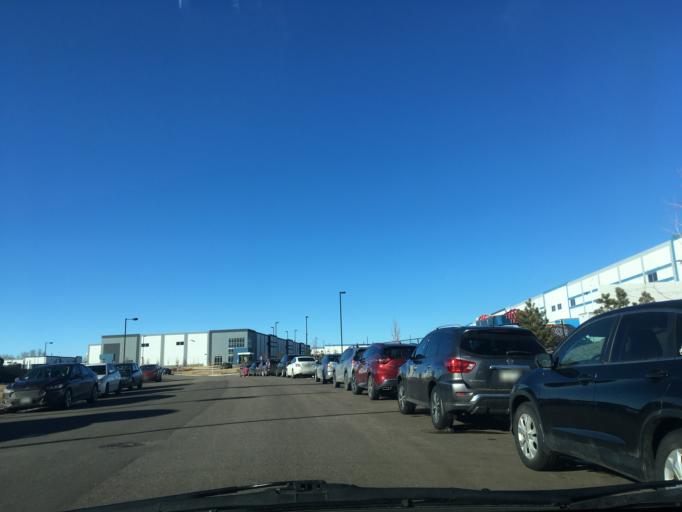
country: US
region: Colorado
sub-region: Adams County
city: Twin Lakes
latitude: 39.7929
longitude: -104.9820
